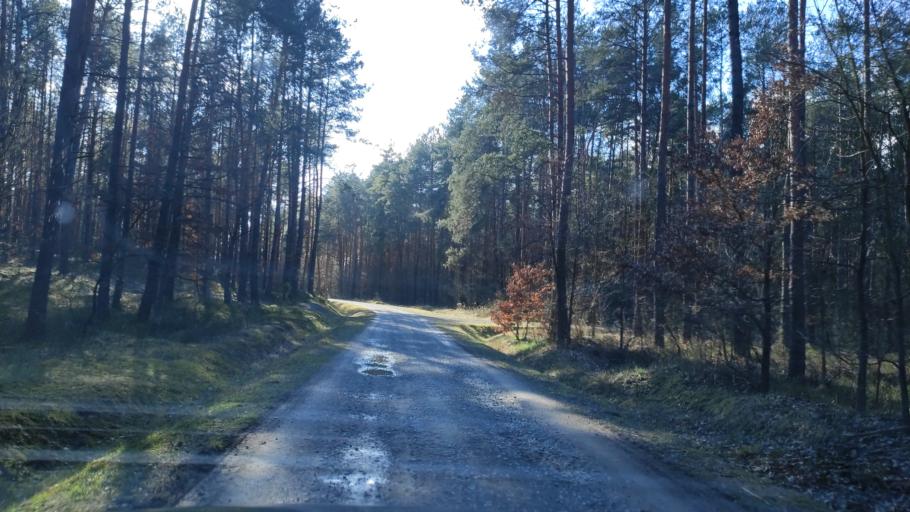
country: PL
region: Masovian Voivodeship
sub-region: Powiat radomski
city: Jastrzebia
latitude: 51.4683
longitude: 21.2359
